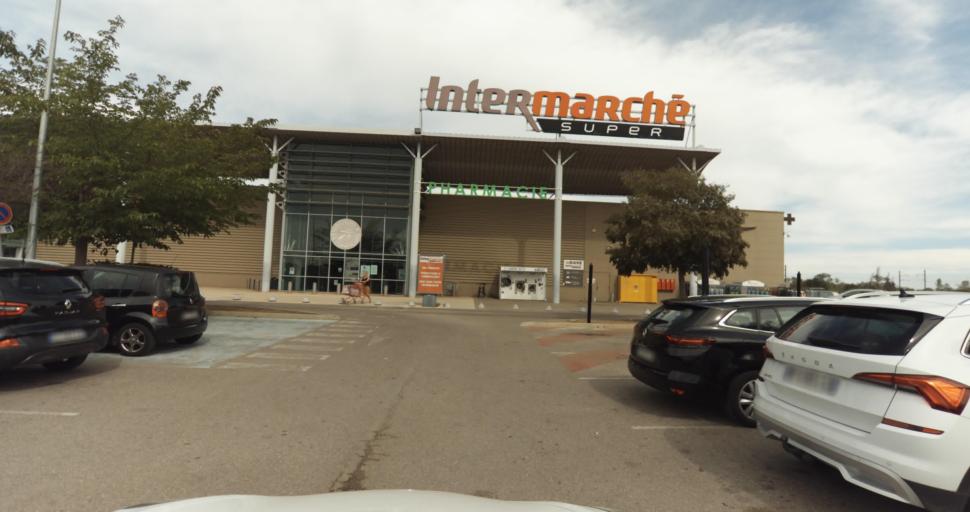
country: FR
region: Provence-Alpes-Cote d'Azur
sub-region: Departement des Bouches-du-Rhone
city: Miramas
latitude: 43.6014
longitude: 5.0046
